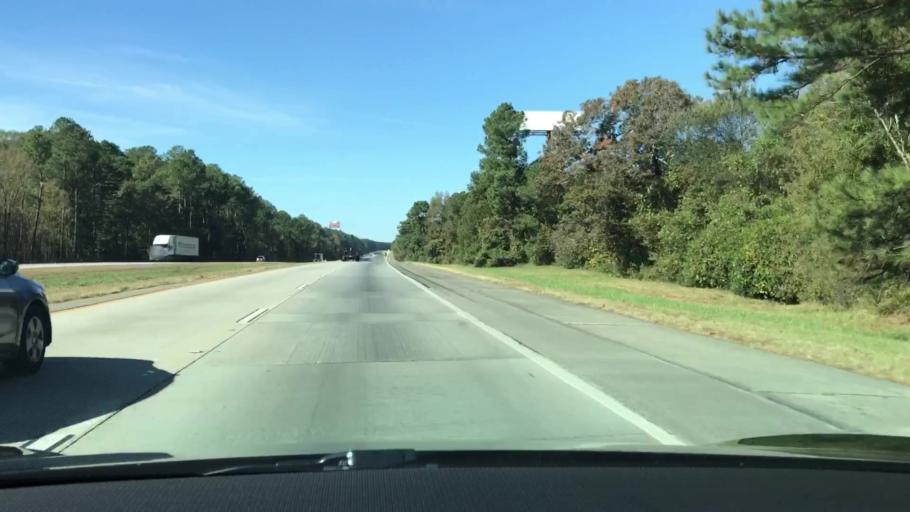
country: US
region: Georgia
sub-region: Taliaferro County
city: Crawfordville
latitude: 33.5282
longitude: -82.9586
